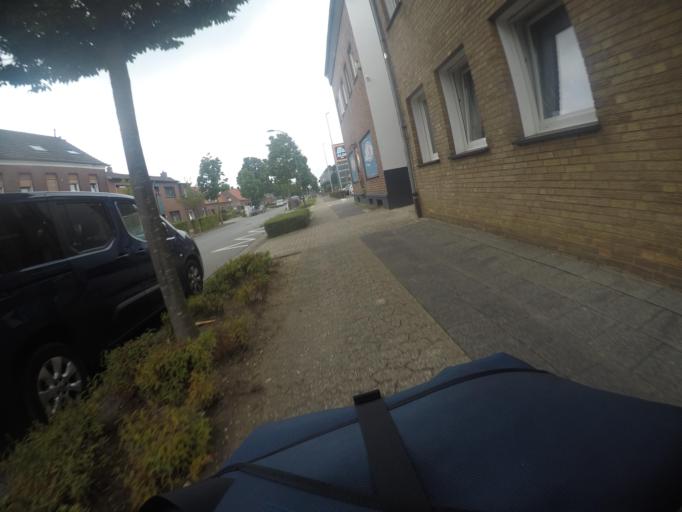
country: DE
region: North Rhine-Westphalia
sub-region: Regierungsbezirk Dusseldorf
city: Kevelaer
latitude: 51.5889
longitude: 6.2400
